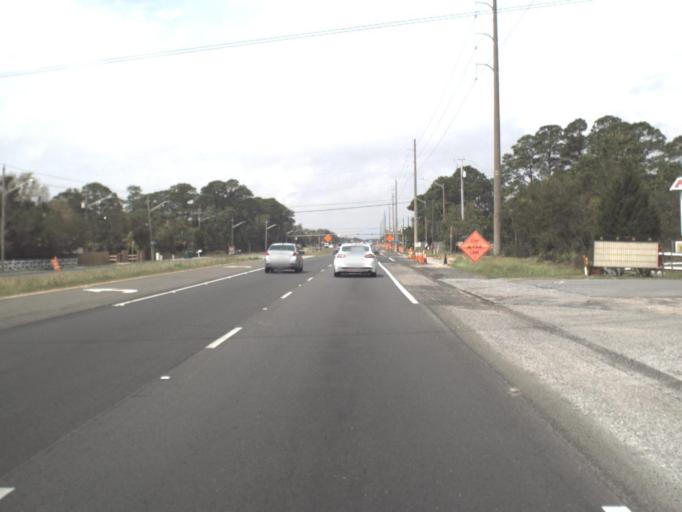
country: US
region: Florida
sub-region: Santa Rosa County
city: Navarre
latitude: 30.4097
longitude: -86.8072
